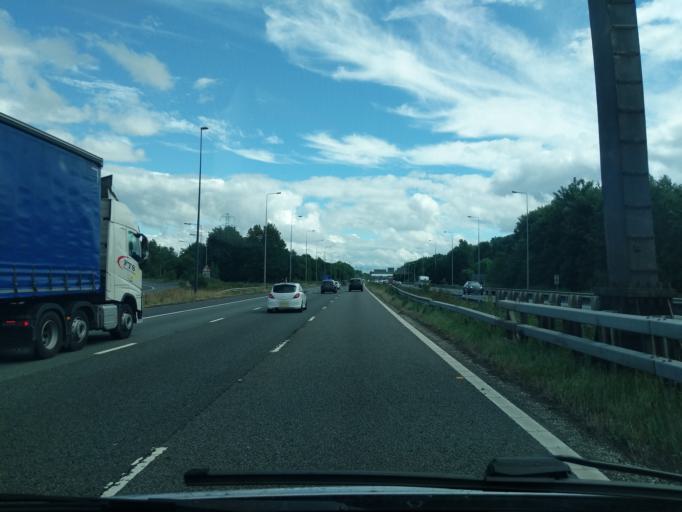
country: GB
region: England
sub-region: Warrington
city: Croft
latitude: 53.4249
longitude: -2.5542
